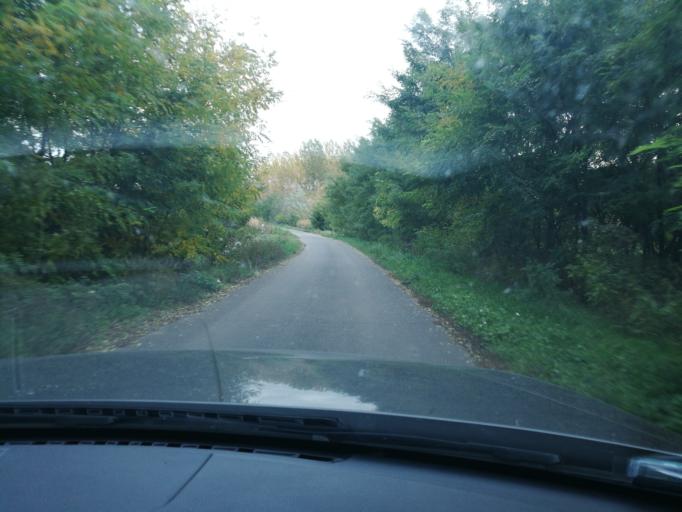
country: HU
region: Szabolcs-Szatmar-Bereg
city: Apagy
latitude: 47.9926
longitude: 21.8899
